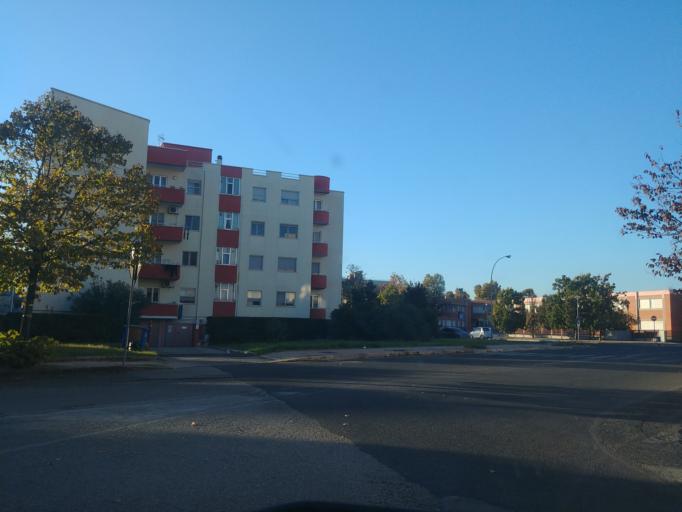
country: IT
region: Latium
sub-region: Provincia di Latina
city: Latina
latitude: 41.4505
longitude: 12.8933
